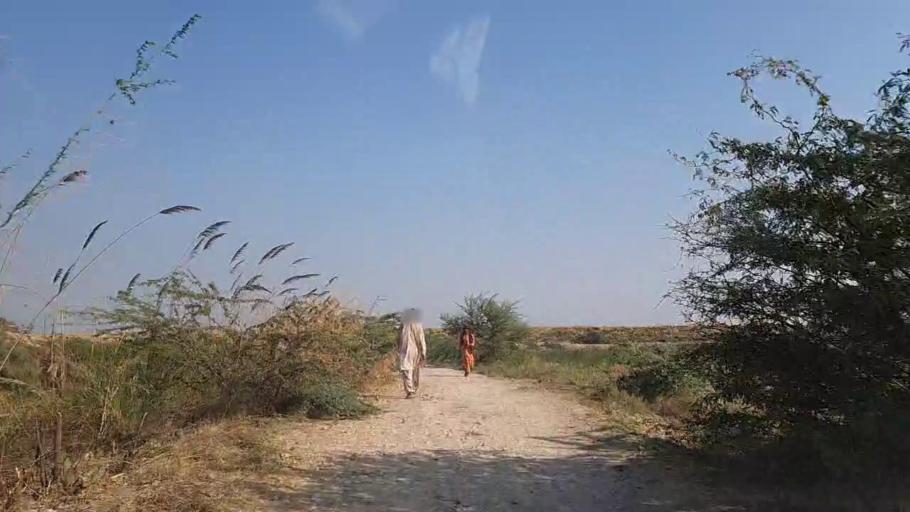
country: PK
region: Sindh
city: Thatta
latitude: 24.7390
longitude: 67.9691
